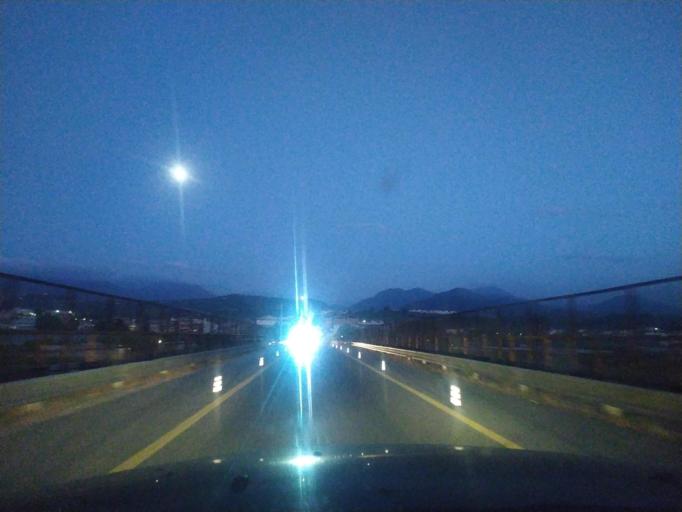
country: IT
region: Sicily
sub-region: Messina
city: Terme
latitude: 38.1420
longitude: 15.1603
